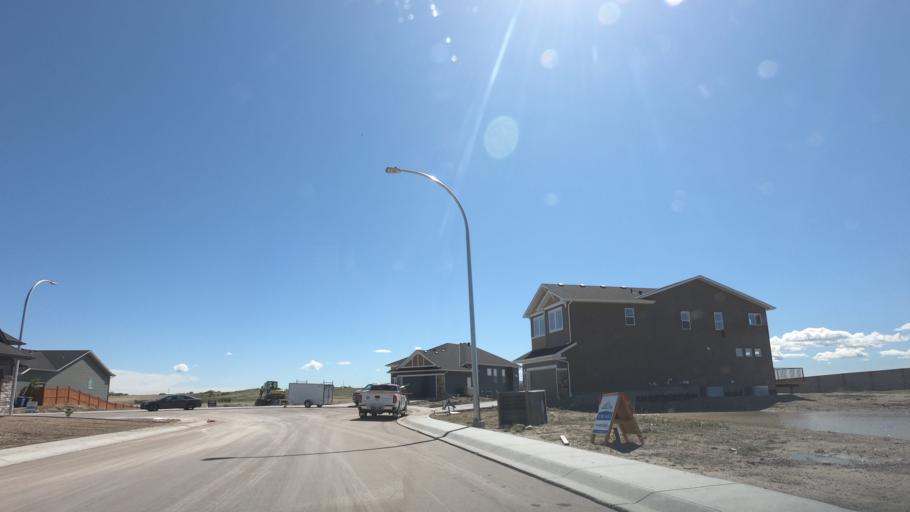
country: CA
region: Alberta
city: Airdrie
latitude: 51.2639
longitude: -113.9714
